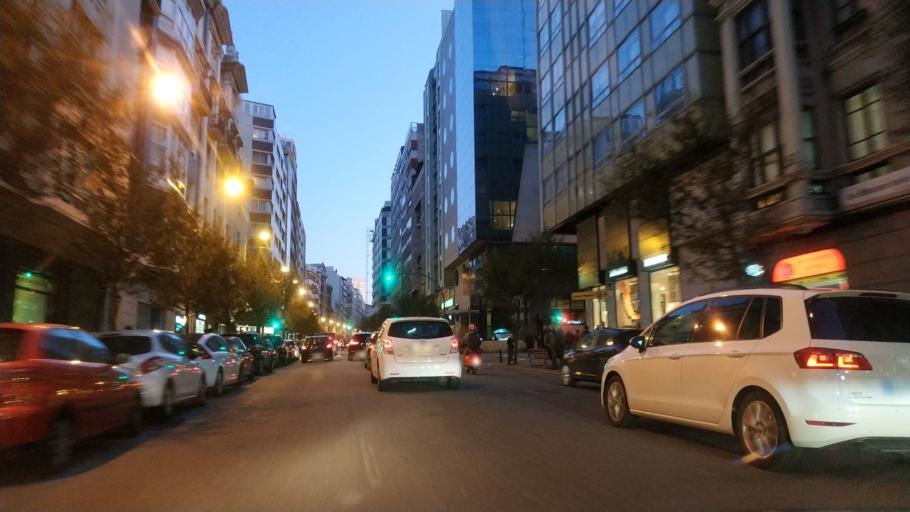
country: ES
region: Galicia
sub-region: Provincia da Coruna
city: A Coruna
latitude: 43.3667
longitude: -8.4086
